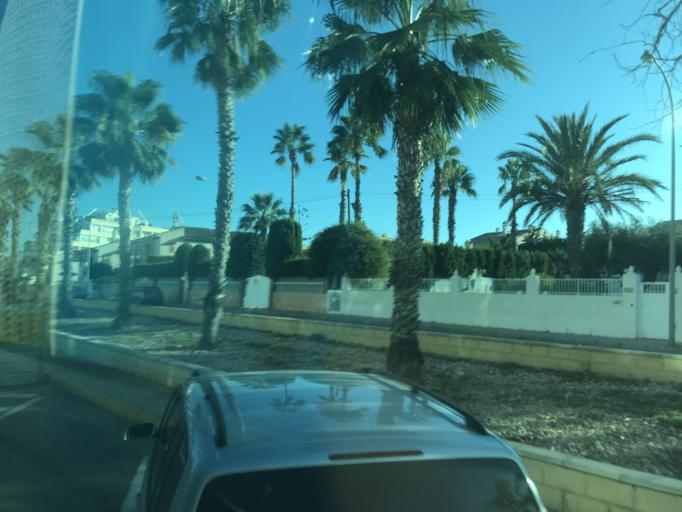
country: ES
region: Valencia
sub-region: Provincia de Alicante
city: Torrevieja
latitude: 38.0043
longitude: -0.6560
